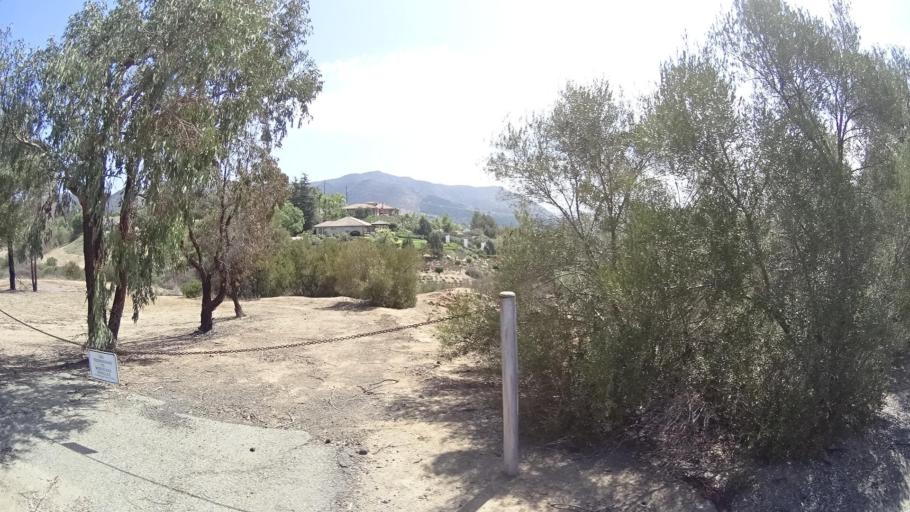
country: US
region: California
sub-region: San Diego County
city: Fallbrook
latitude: 33.4272
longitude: -117.2381
